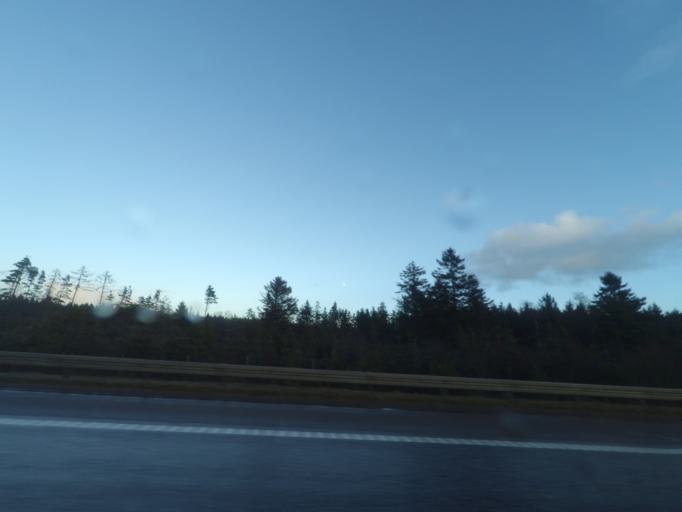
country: DK
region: Central Jutland
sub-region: Herning Kommune
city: Lind
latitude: 56.0464
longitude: 9.0009
